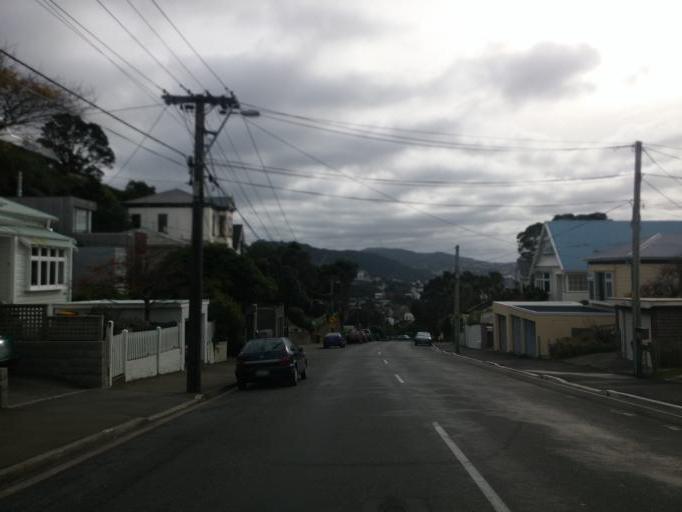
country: NZ
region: Wellington
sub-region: Wellington City
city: Wellington
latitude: -41.3045
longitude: 174.7667
